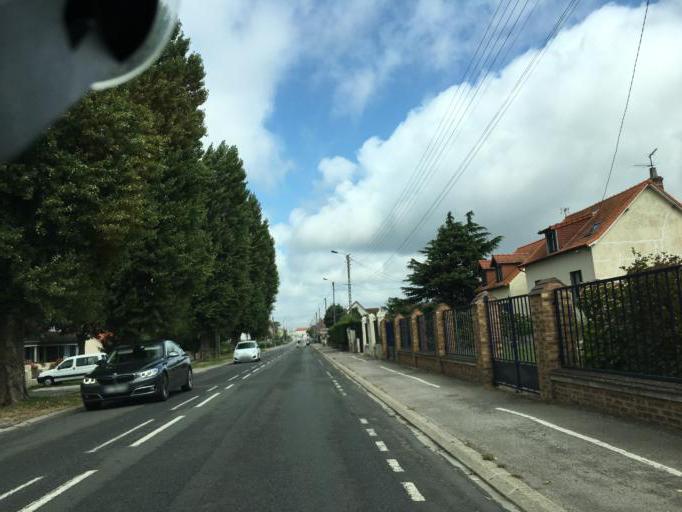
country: FR
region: Nord-Pas-de-Calais
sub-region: Departement du Pas-de-Calais
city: Rang-du-Fliers
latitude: 50.4114
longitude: 1.6476
